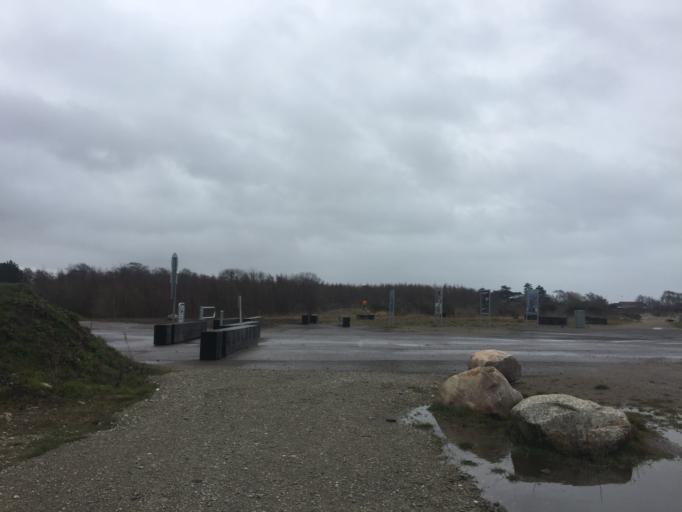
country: DK
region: Zealand
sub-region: Slagelse Kommune
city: Korsor
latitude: 55.3478
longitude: 11.1109
